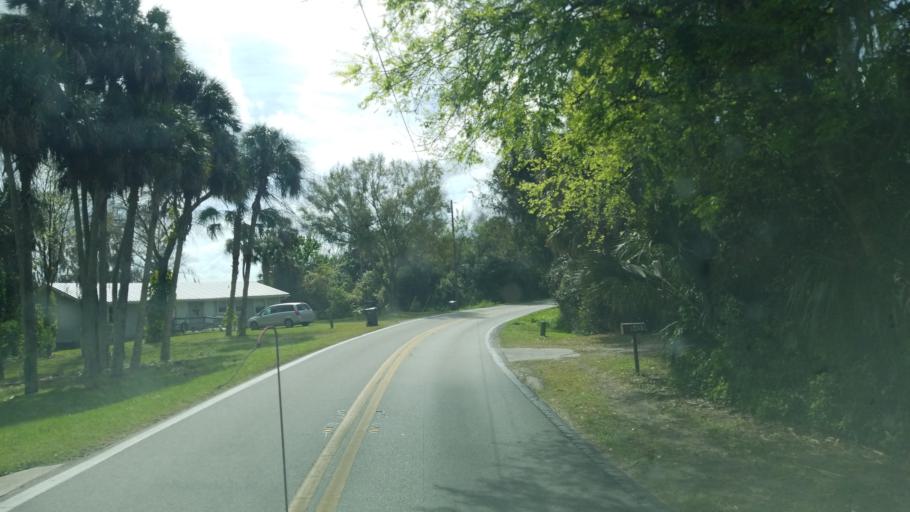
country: US
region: Florida
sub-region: Polk County
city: Dundee
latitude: 27.9898
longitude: -81.5499
